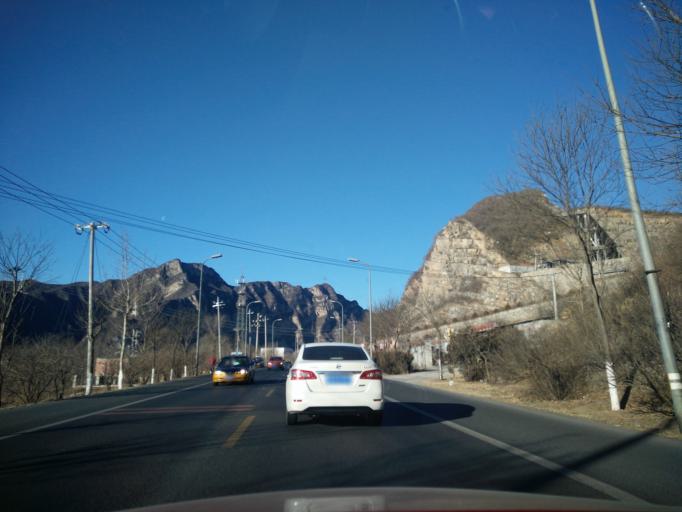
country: CN
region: Beijing
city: Miaofengshan
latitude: 39.9759
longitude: 116.0518
